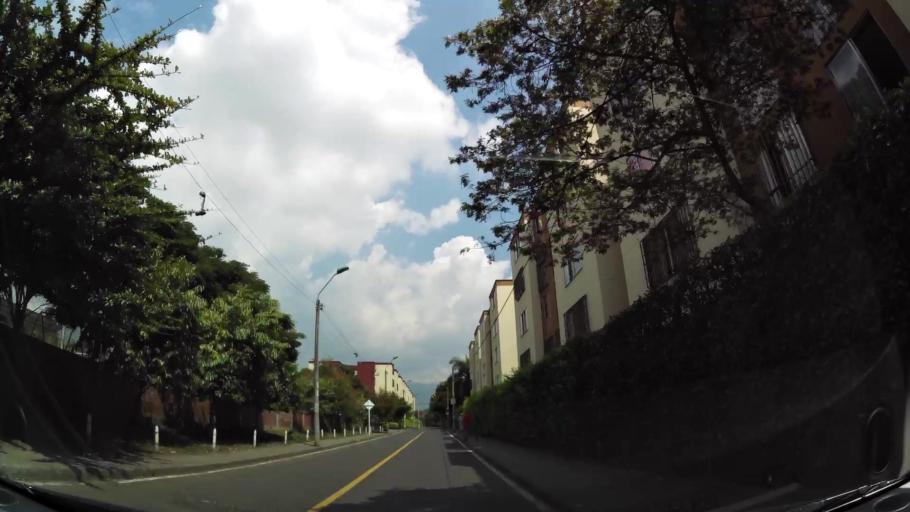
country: CO
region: Valle del Cauca
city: Cali
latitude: 3.4932
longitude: -76.5048
